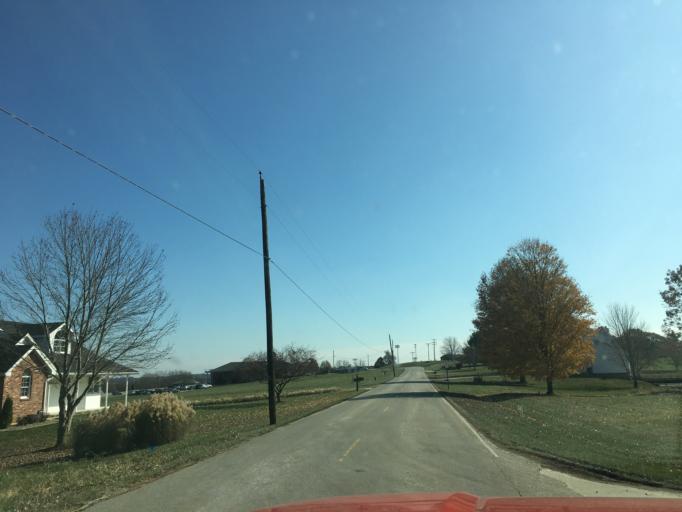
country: US
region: Missouri
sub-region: Cole County
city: Wardsville
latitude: 38.4988
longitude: -92.1813
